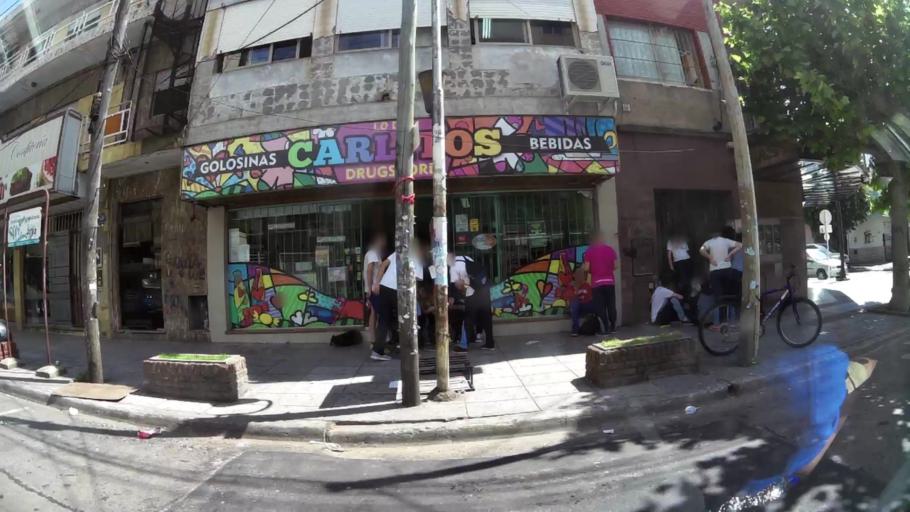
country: AR
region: Buenos Aires
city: San Justo
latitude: -34.6784
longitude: -58.5626
